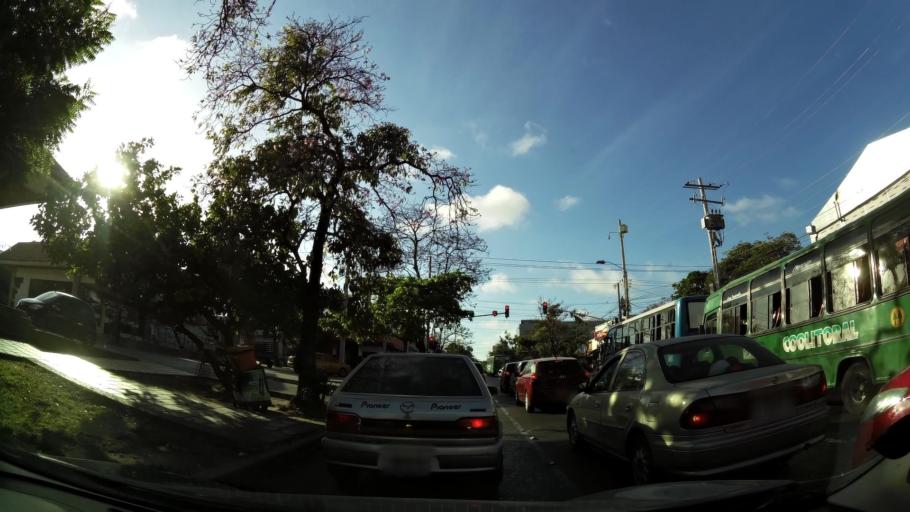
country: CO
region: Atlantico
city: Barranquilla
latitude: 10.9902
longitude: -74.8046
